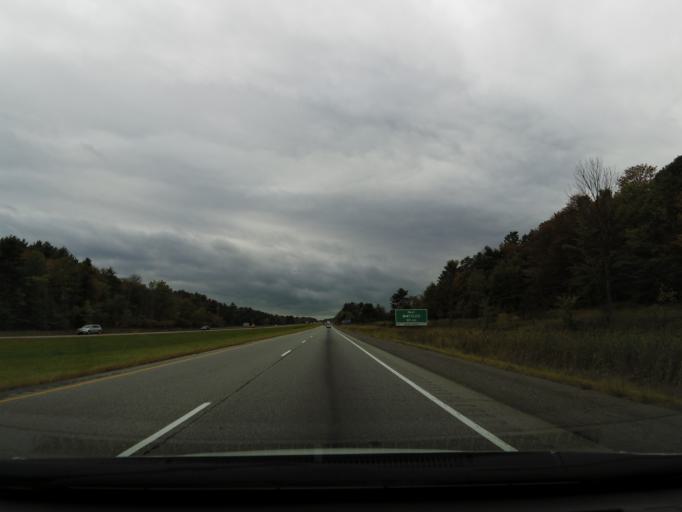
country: US
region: New York
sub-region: Jefferson County
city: Alexandria Bay
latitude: 44.4984
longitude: -75.8454
